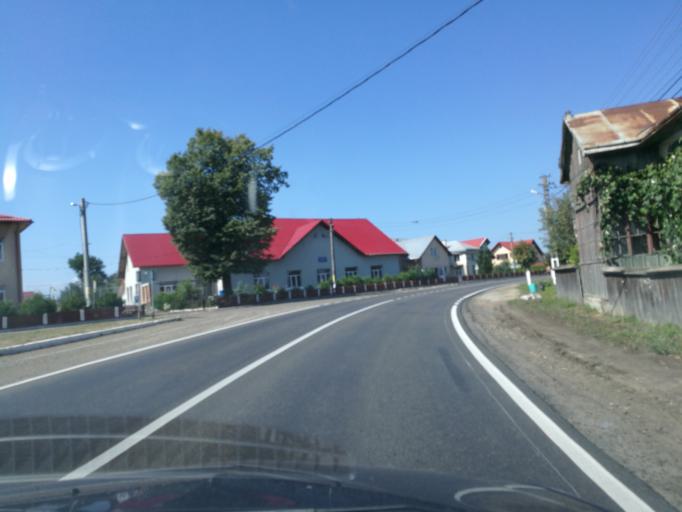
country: RO
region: Suceava
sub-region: Comuna Milisauti
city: Badeuti
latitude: 47.8027
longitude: 25.9822
